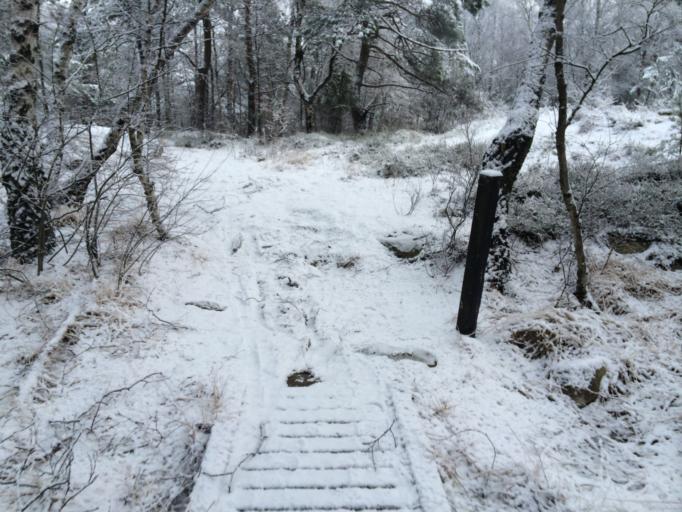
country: SE
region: Vaestra Goetaland
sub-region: Goteborg
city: Majorna
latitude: 57.7210
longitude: 11.8836
